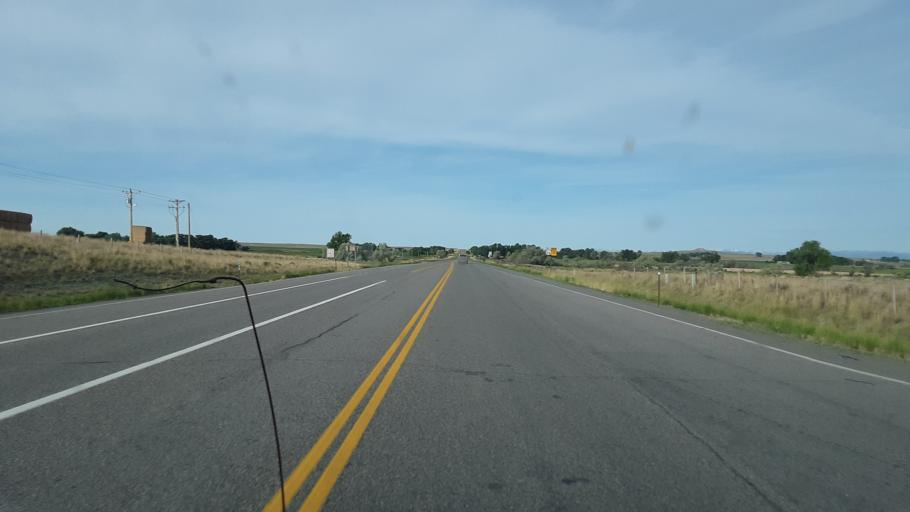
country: US
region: Wyoming
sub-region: Fremont County
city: Riverton
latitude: 43.1856
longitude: -108.2458
